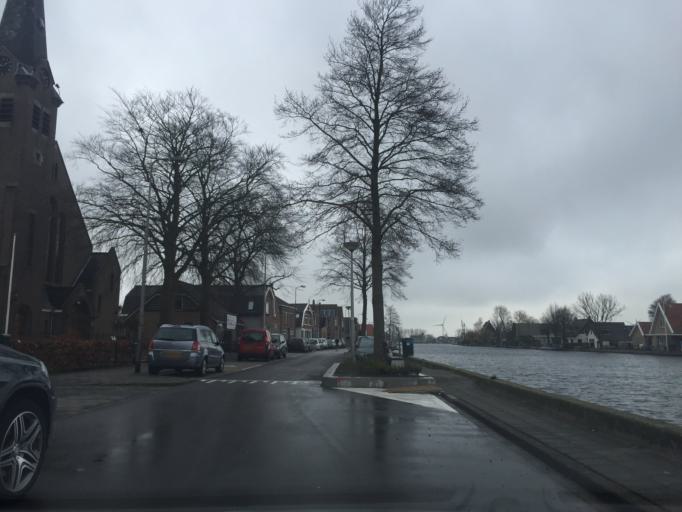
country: NL
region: South Holland
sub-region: Gemeente Kaag en Braassem
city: Oude Wetering
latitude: 52.2147
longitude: 4.6456
